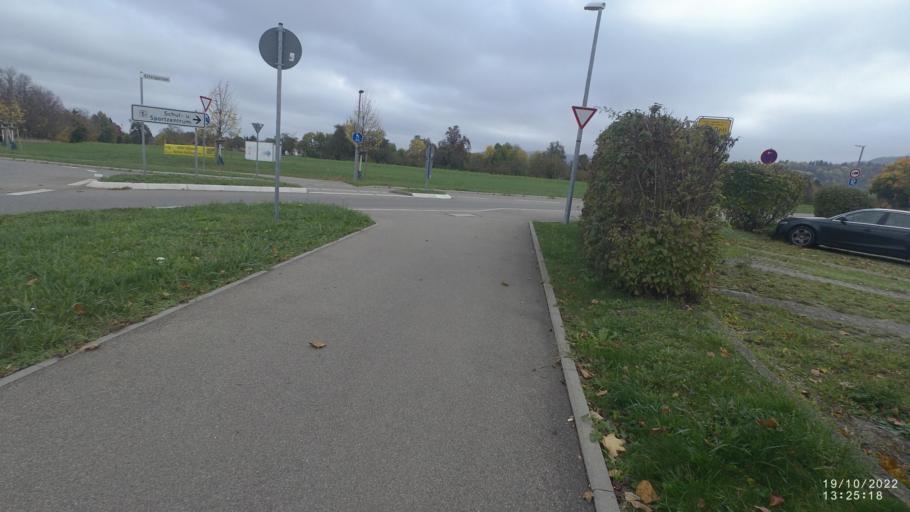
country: DE
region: Baden-Wuerttemberg
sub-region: Regierungsbezirk Stuttgart
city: Boll
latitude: 48.6435
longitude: 9.6062
